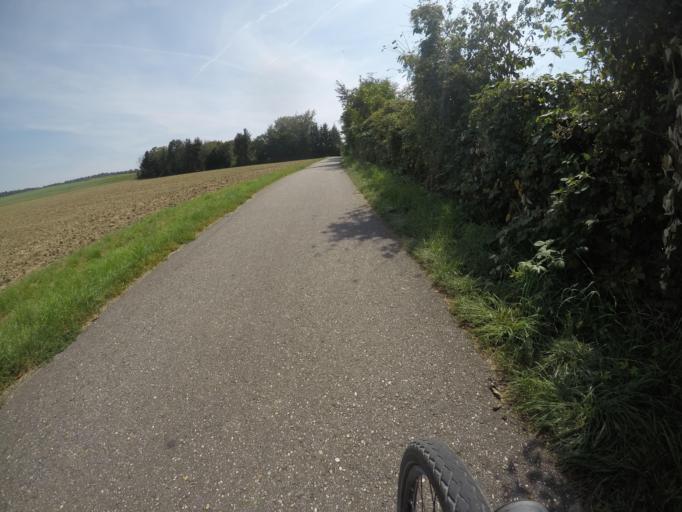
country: DE
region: Baden-Wuerttemberg
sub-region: Karlsruhe Region
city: Gondelsheim
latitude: 49.0696
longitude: 8.6630
